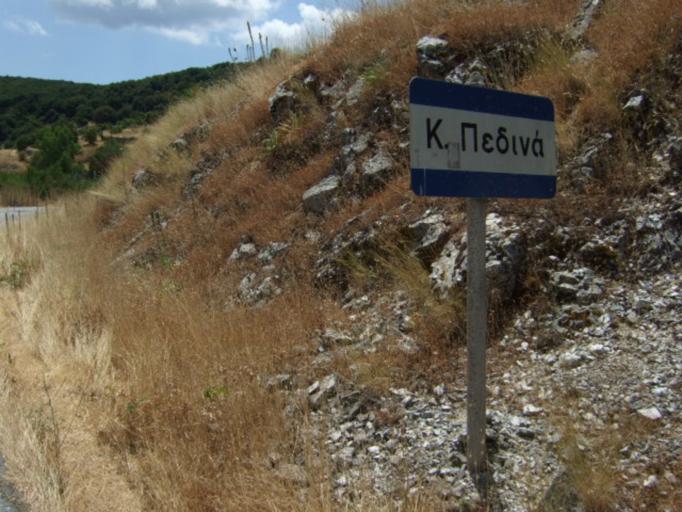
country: GR
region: Epirus
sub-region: Nomos Ioanninon
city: Kalpaki
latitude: 39.8818
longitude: 20.6770
